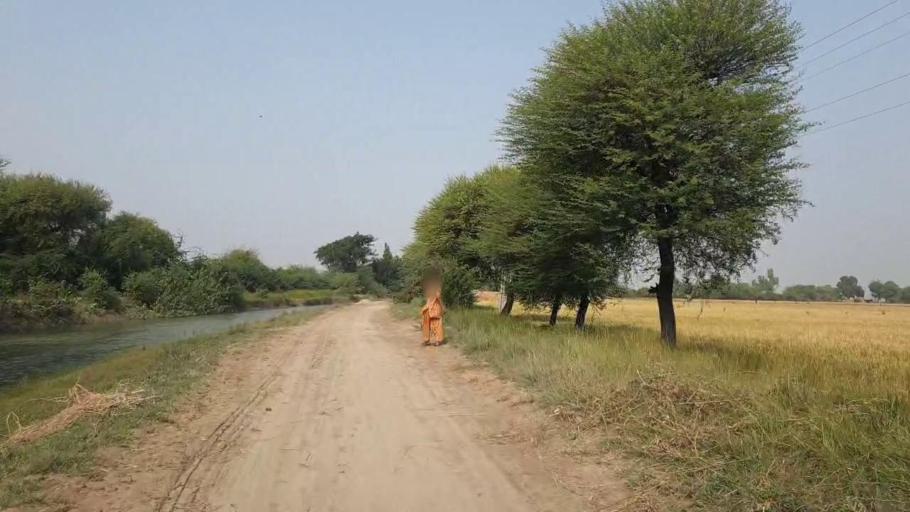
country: PK
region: Sindh
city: Kario
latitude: 24.8317
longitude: 68.5453
